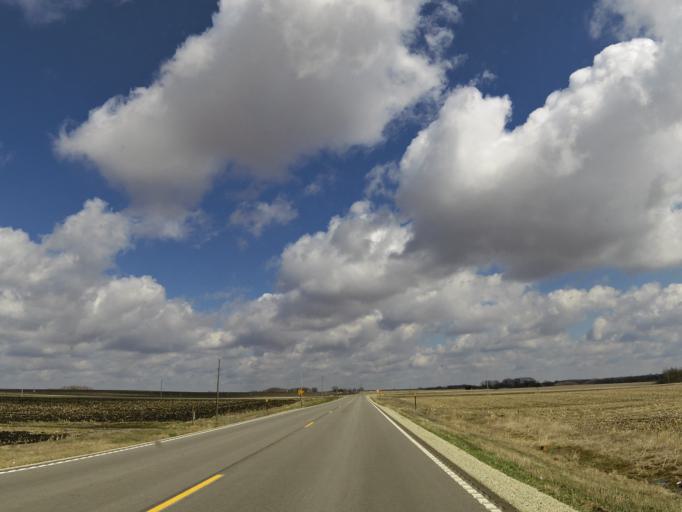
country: US
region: Minnesota
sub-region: Dodge County
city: Dodge Center
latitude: 44.0879
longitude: -92.8524
